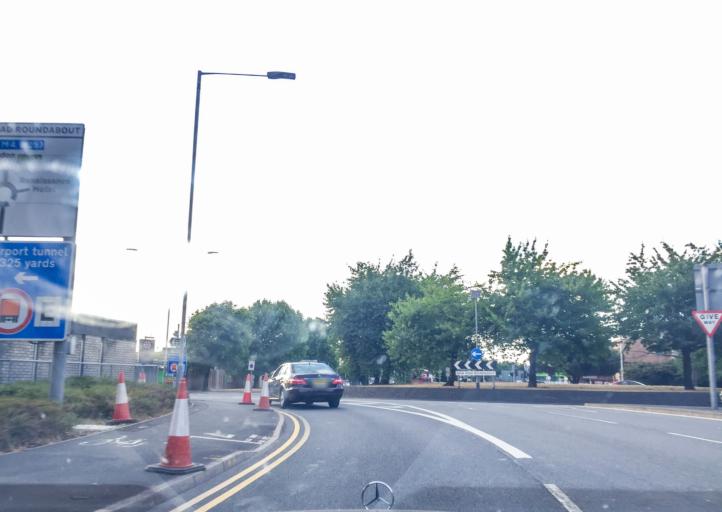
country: GB
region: England
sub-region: Greater London
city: West Drayton
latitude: 51.4801
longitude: -0.4497
